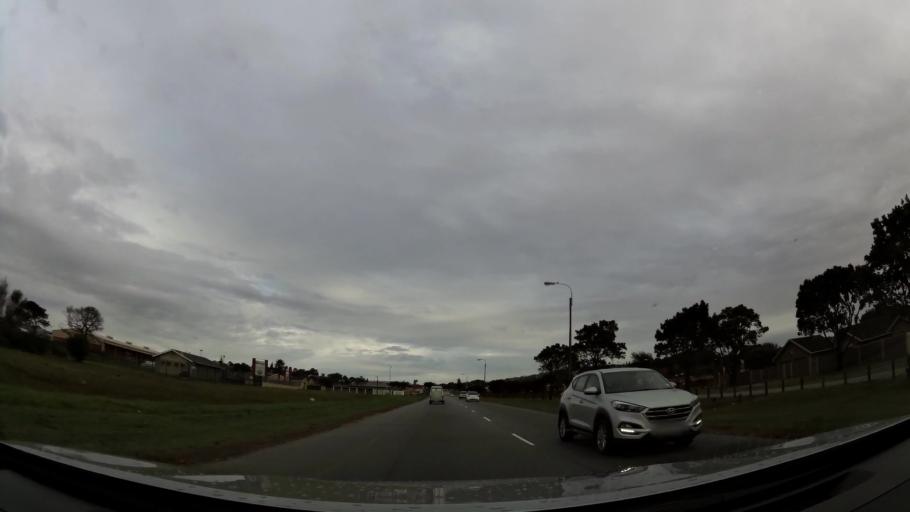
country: ZA
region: Eastern Cape
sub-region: Nelson Mandela Bay Metropolitan Municipality
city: Port Elizabeth
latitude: -33.9931
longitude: 25.5436
